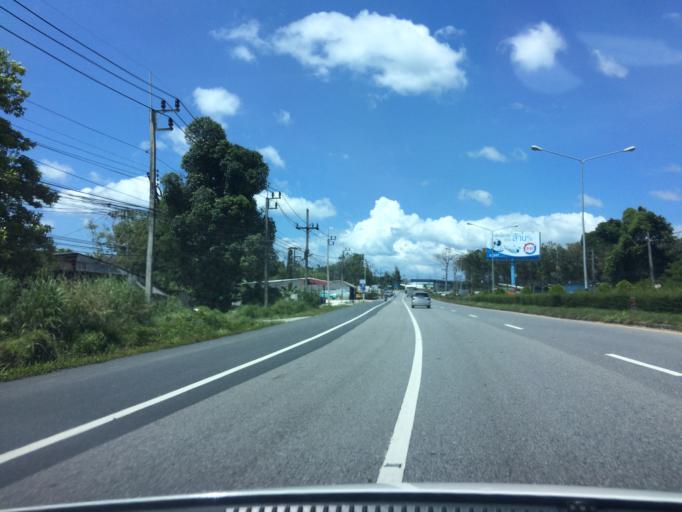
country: TH
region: Phangnga
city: Thai Mueang
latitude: 8.2286
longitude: 98.2998
